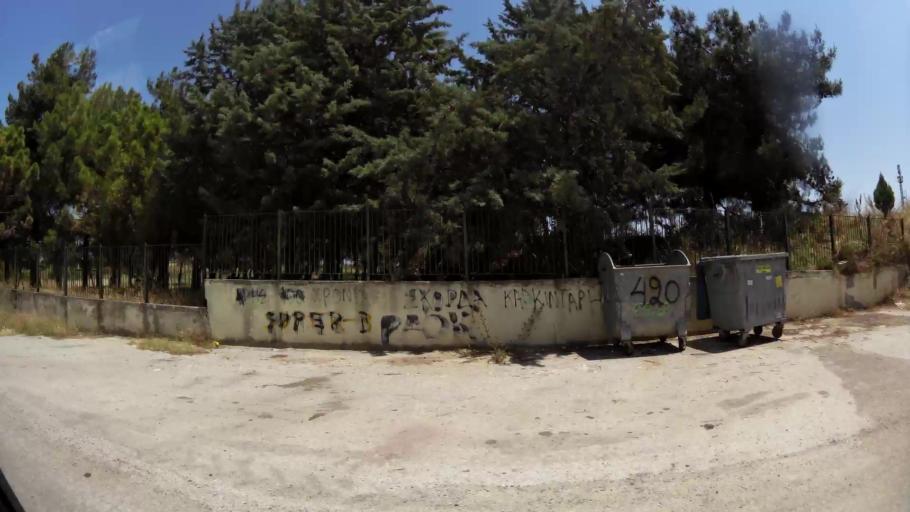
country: GR
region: Central Macedonia
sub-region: Nomos Thessalonikis
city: Epanomi
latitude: 40.4258
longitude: 22.9353
